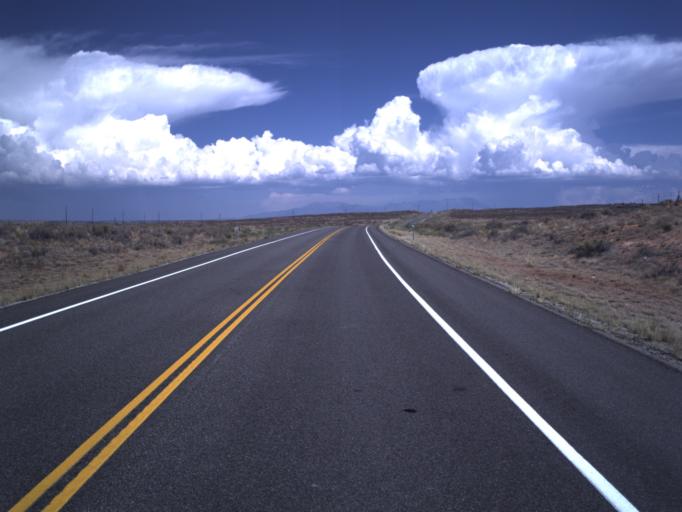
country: US
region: Utah
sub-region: San Juan County
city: Blanding
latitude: 37.3366
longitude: -109.5199
